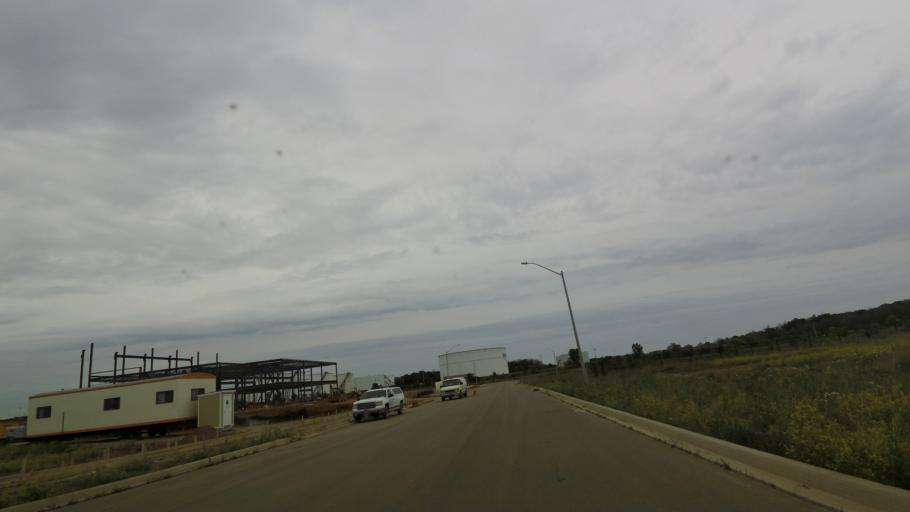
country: CA
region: Ontario
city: Oakville
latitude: 43.3879
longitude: -79.7364
